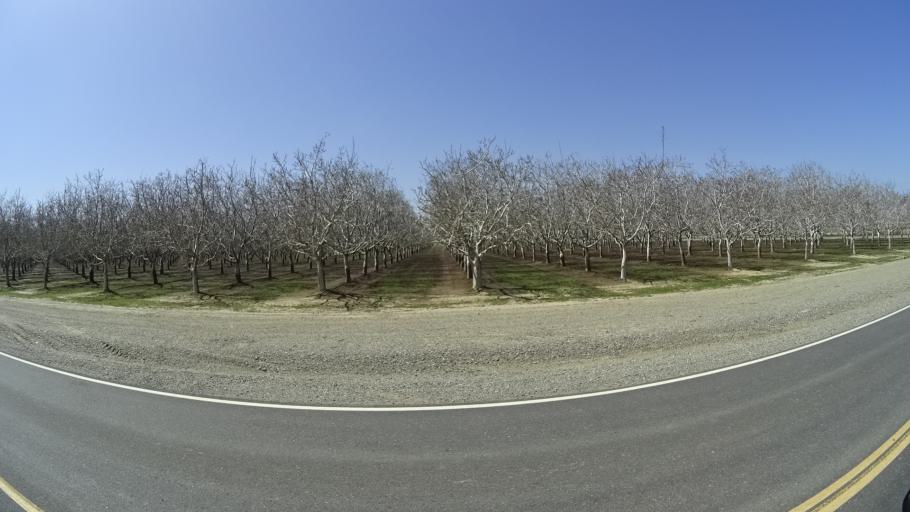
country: US
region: California
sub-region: Glenn County
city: Willows
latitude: 39.6103
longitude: -122.1376
